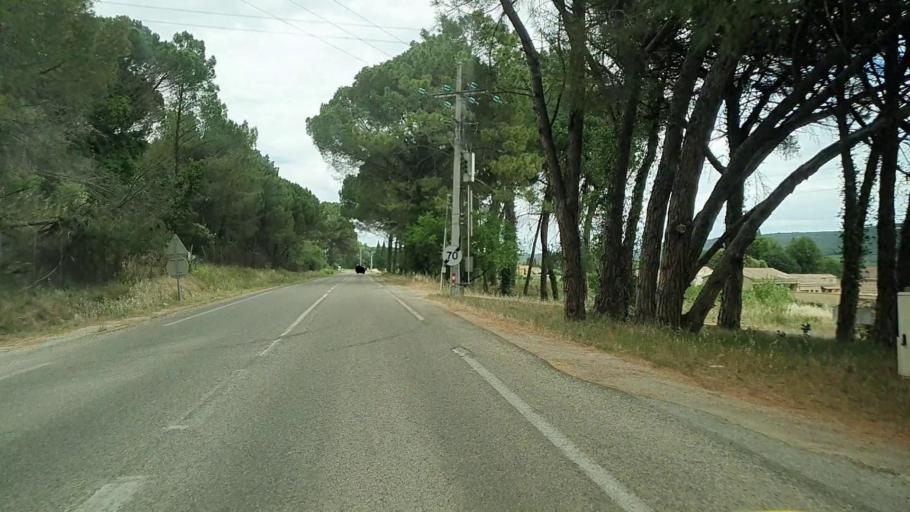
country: FR
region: Languedoc-Roussillon
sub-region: Departement du Gard
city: Tresques
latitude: 44.1182
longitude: 4.5950
